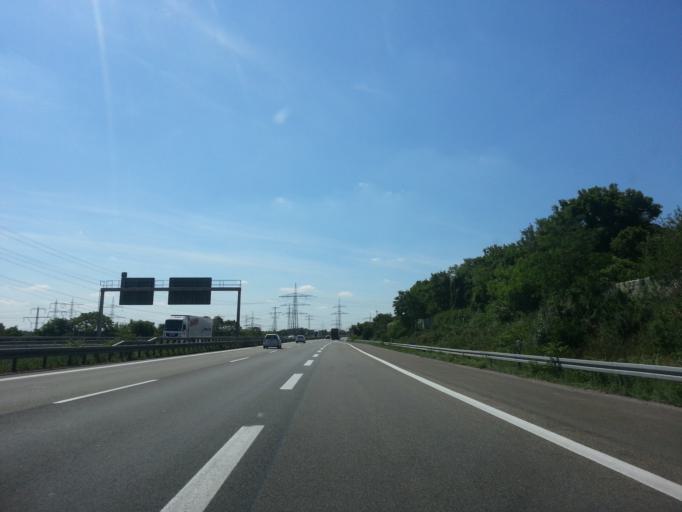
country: DE
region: Baden-Wuerttemberg
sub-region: Karlsruhe Region
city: Ilvesheim
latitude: 49.4568
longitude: 8.5409
